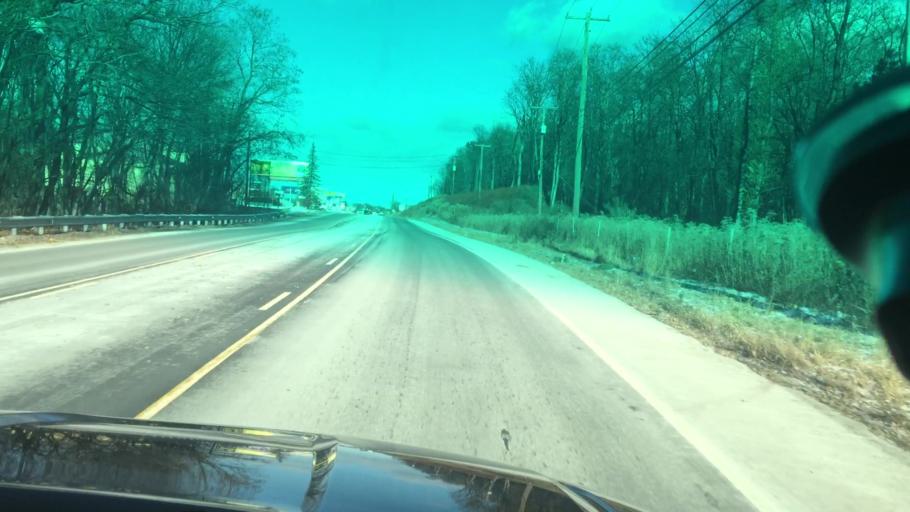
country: US
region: Pennsylvania
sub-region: Luzerne County
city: Georgetown
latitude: 41.2257
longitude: -75.8768
